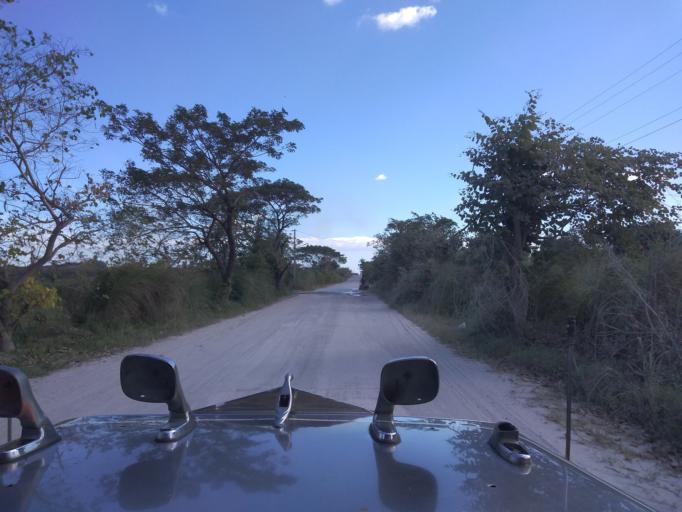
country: PH
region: Central Luzon
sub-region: Province of Pampanga
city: Magliman
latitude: 15.0363
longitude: 120.6324
